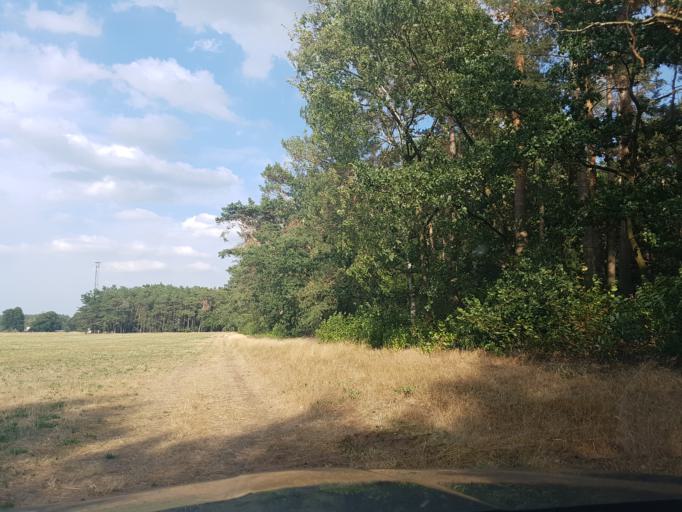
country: DE
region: Brandenburg
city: Schilda
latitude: 51.5745
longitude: 13.3505
